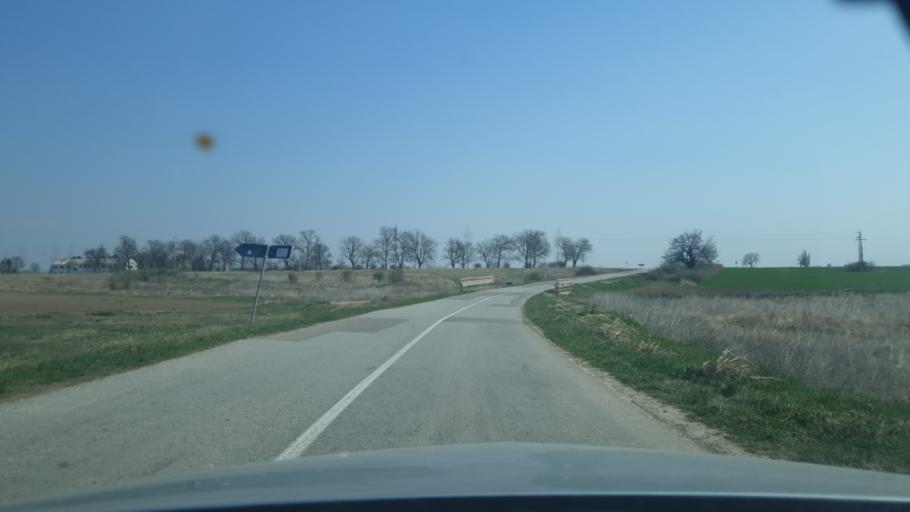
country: RS
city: Sasinci
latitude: 45.0476
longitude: 19.7186
